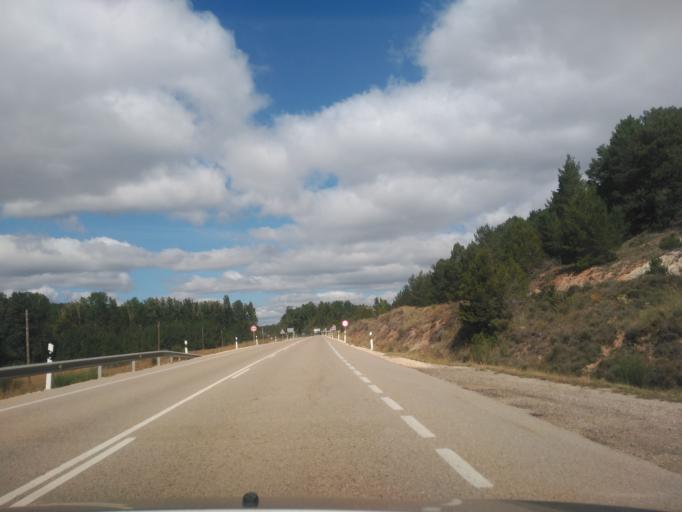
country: ES
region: Castille and Leon
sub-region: Provincia de Burgos
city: Hontoria del Pinar
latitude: 41.8559
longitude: -3.1926
